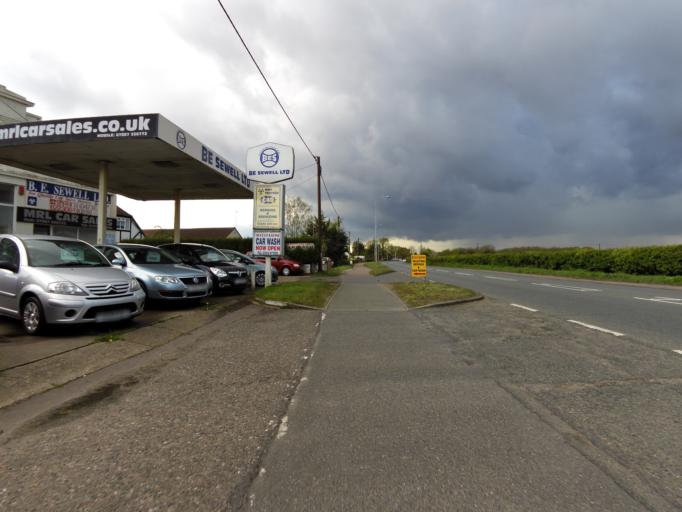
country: GB
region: England
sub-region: Suffolk
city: Kesgrave
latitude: 52.0650
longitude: 1.2267
